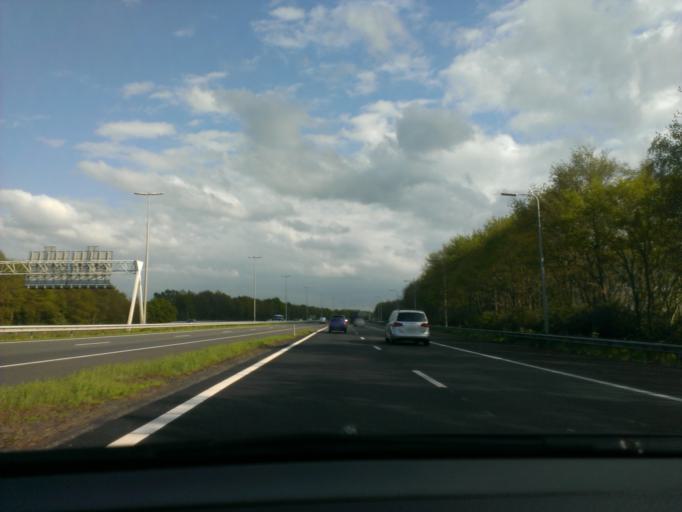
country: NL
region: Gelderland
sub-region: Gemeente Hattem
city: Hattem
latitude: 52.4826
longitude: 6.0284
